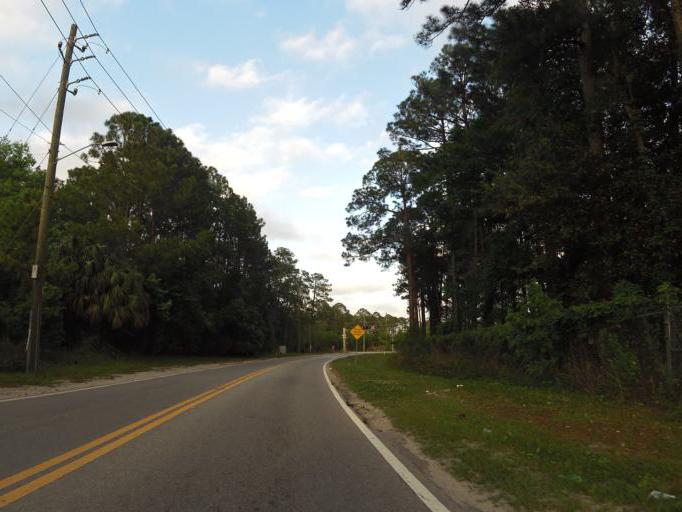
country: US
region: Florida
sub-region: Duval County
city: Jacksonville
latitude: 30.4481
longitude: -81.6376
